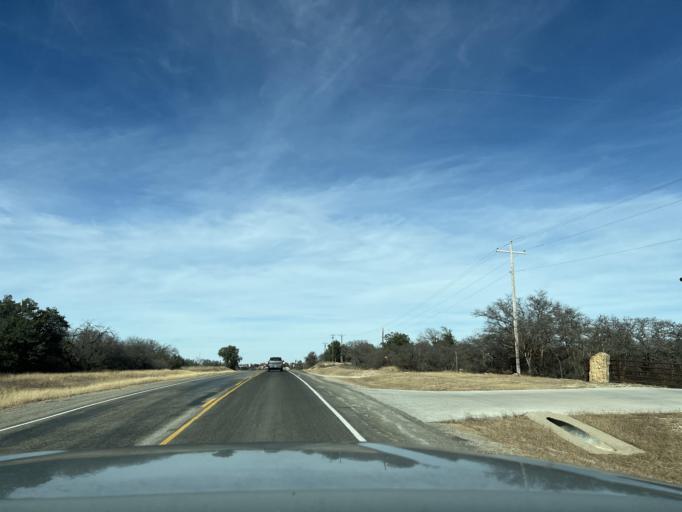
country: US
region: Texas
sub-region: Eastland County
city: Cisco
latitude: 32.4197
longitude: -98.9871
